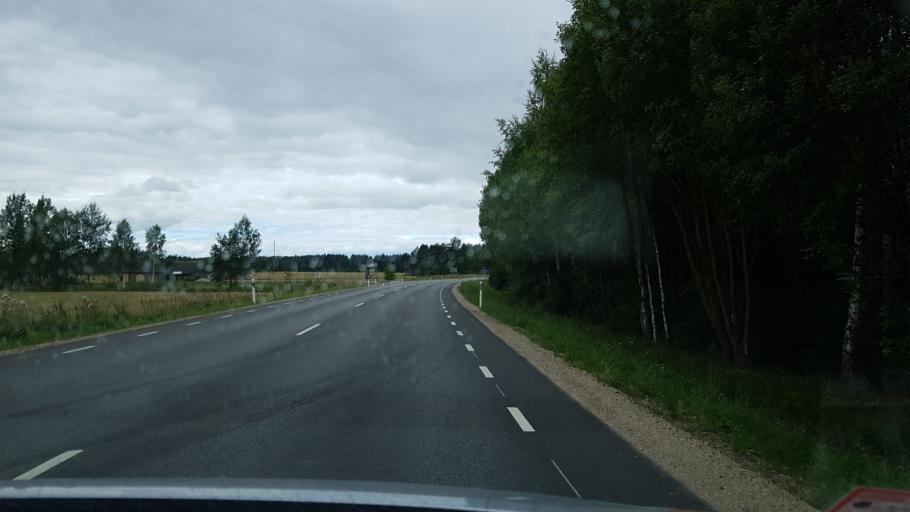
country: EE
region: Polvamaa
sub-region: Raepina vald
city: Rapina
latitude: 58.0712
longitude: 27.2784
